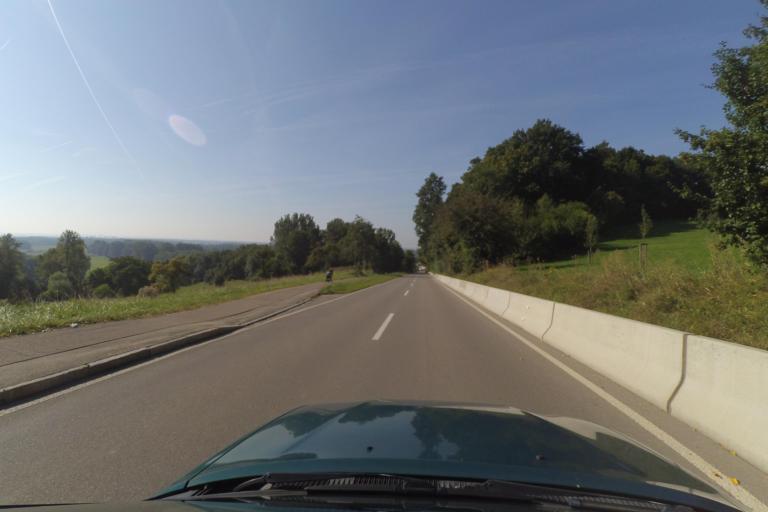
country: DE
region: Bavaria
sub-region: Swabia
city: Genderkingen
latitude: 48.7416
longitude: 10.8808
